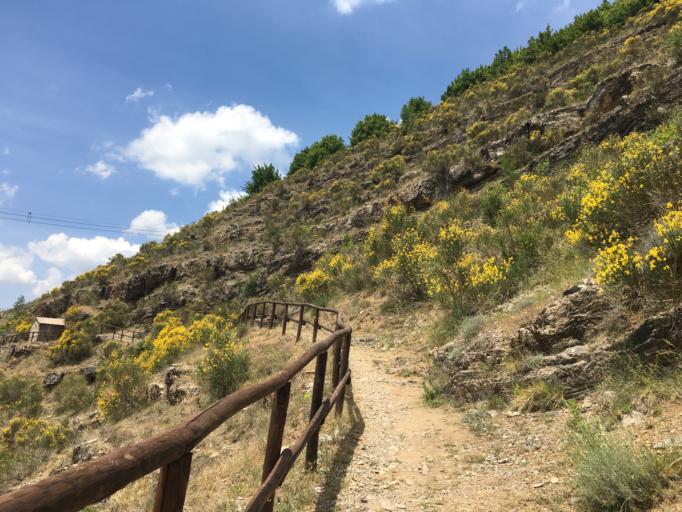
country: IT
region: Basilicate
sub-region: Provincia di Potenza
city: Sasso di Castalda
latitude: 40.4918
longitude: 15.6751
